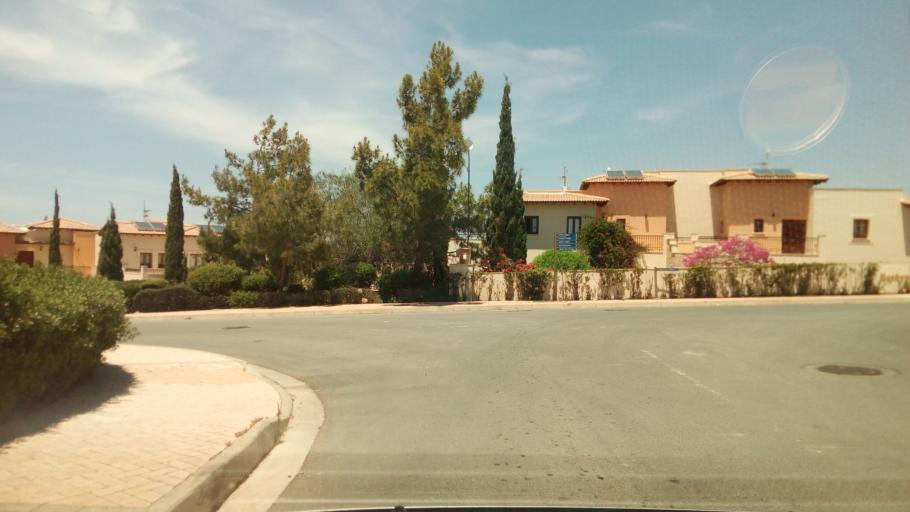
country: CY
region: Limassol
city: Pissouri
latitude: 34.6874
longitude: 32.6024
